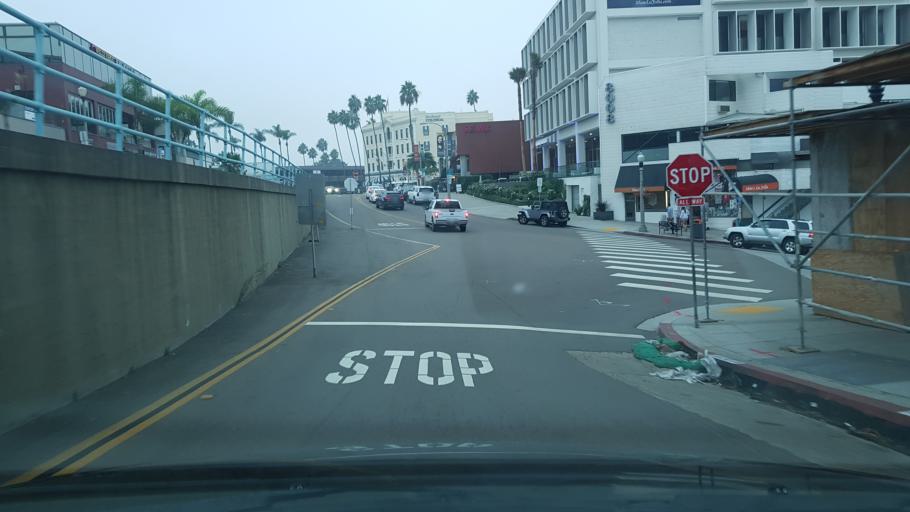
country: US
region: California
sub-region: San Diego County
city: La Jolla
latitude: 32.8482
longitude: -117.2739
